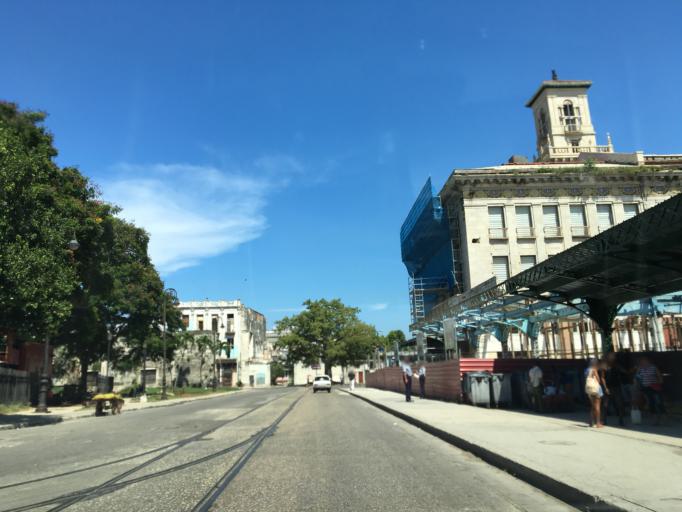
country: CU
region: La Habana
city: La Habana Vieja
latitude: 23.1301
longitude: -82.3553
